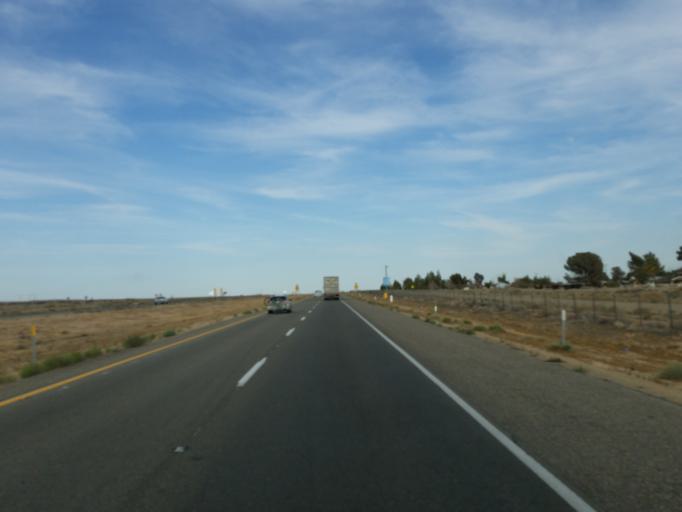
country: US
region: California
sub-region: Kern County
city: Boron
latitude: 35.0101
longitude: -117.6433
